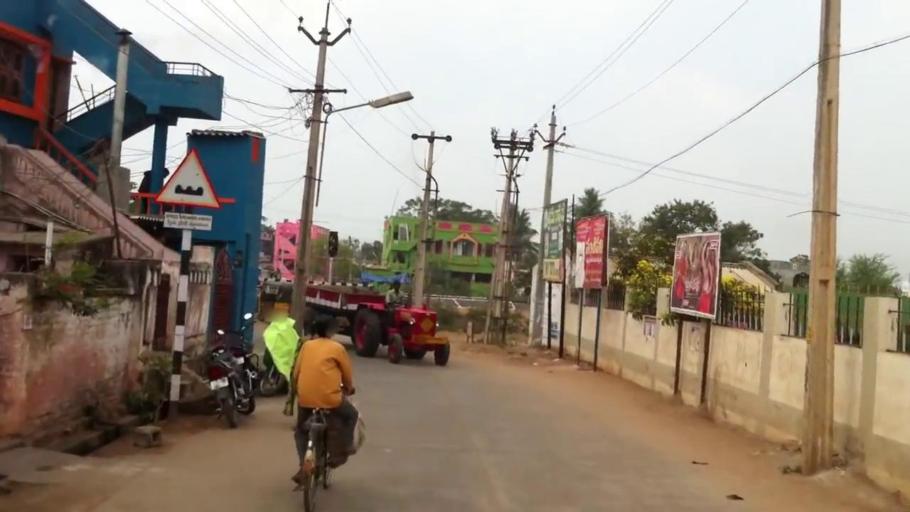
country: IN
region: Andhra Pradesh
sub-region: Guntur
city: Bhattiprolu
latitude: 16.2266
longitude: 80.6527
